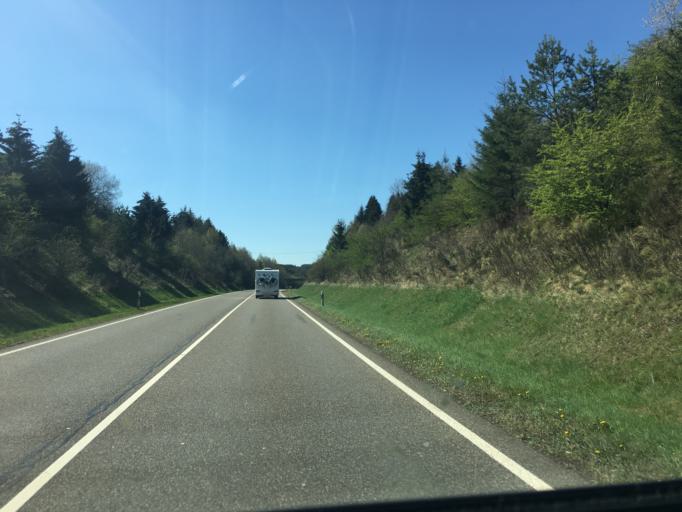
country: DE
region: Rheinland-Pfalz
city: Oberlauch
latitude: 50.1823
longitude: 6.4173
